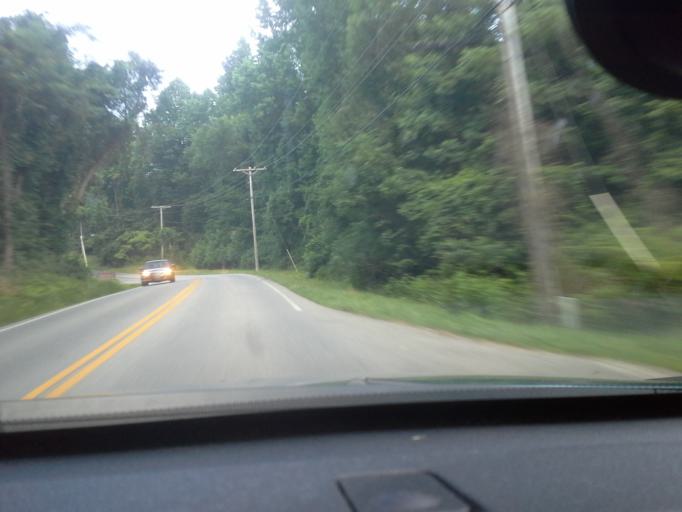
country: US
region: Maryland
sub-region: Calvert County
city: Prince Frederick
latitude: 38.5711
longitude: -76.5369
